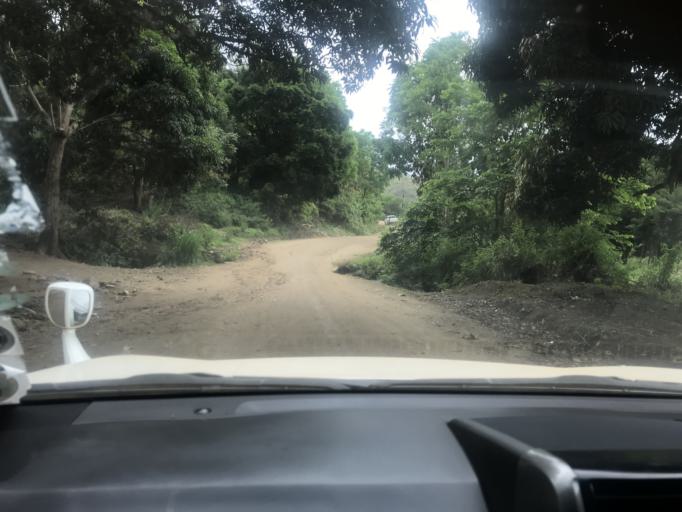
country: TZ
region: Morogoro
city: Morogoro
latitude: -6.9963
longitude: 37.5712
